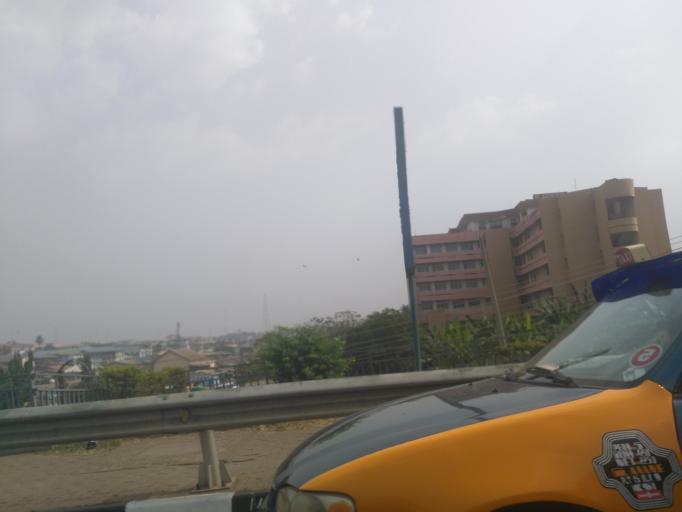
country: GH
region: Ashanti
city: Kumasi
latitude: 6.6885
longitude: -1.6181
